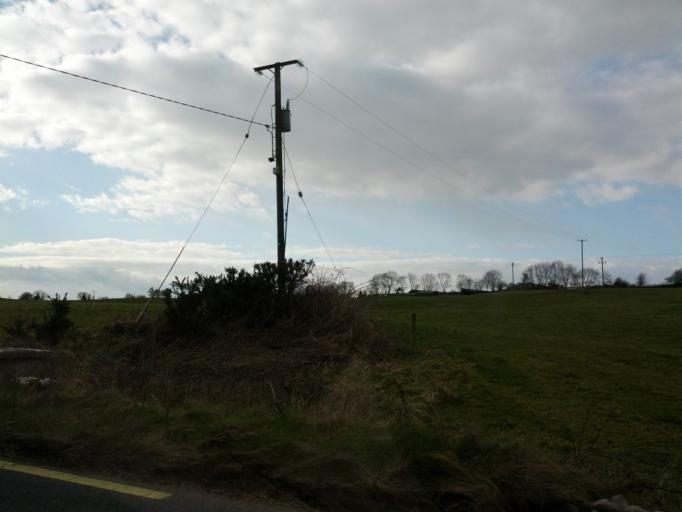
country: IE
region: Connaught
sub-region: County Galway
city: Athenry
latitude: 53.4600
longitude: -8.6740
